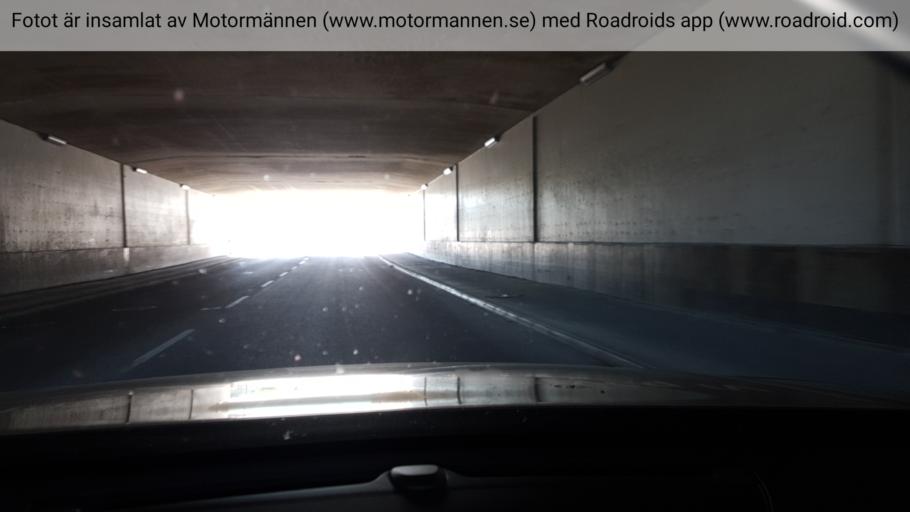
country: SE
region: Stockholm
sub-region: Stockholms Kommun
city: Arsta
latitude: 59.2636
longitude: 18.0425
